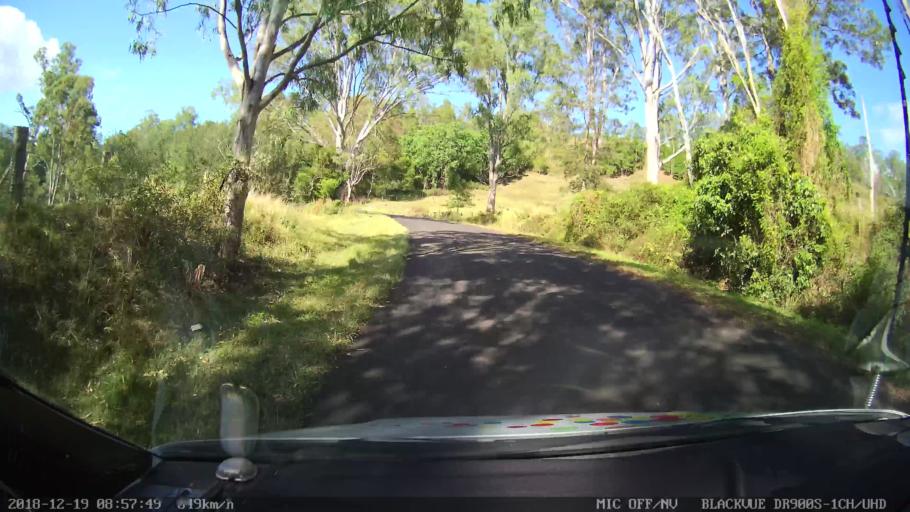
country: AU
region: New South Wales
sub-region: Kyogle
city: Kyogle
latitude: -28.4215
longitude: 152.9689
